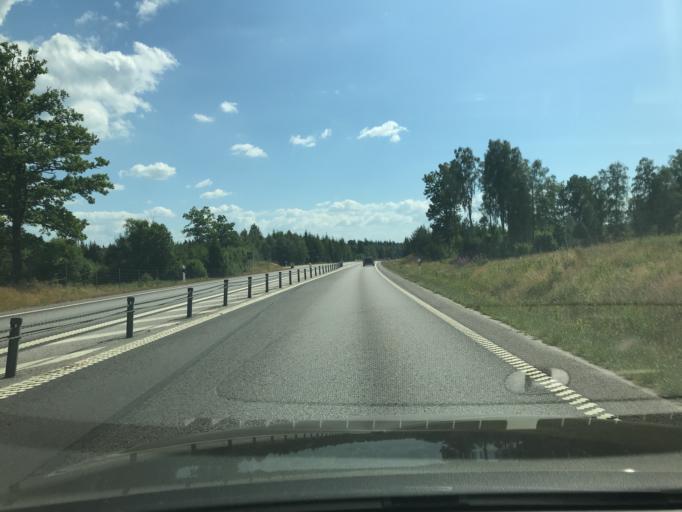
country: SE
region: Kronoberg
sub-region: Almhults Kommun
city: AElmhult
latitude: 56.5245
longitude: 14.1407
